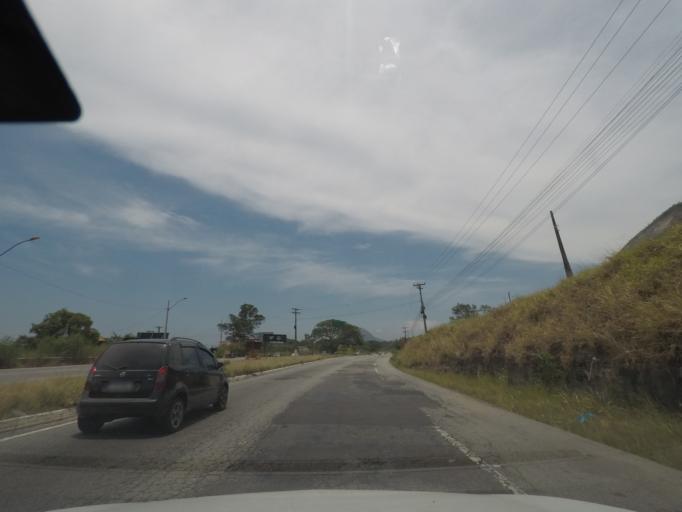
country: BR
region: Rio de Janeiro
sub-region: Marica
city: Marica
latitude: -22.9356
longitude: -42.9047
